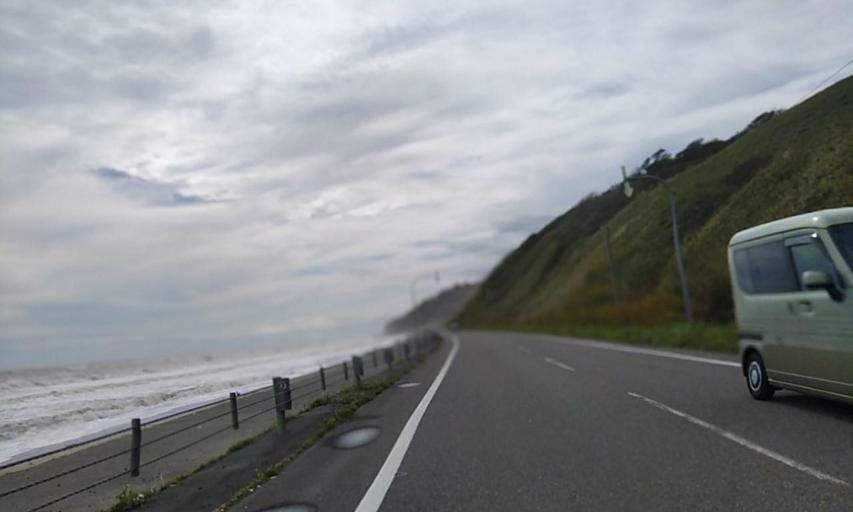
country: JP
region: Hokkaido
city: Obihiro
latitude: 42.7799
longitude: 143.7827
